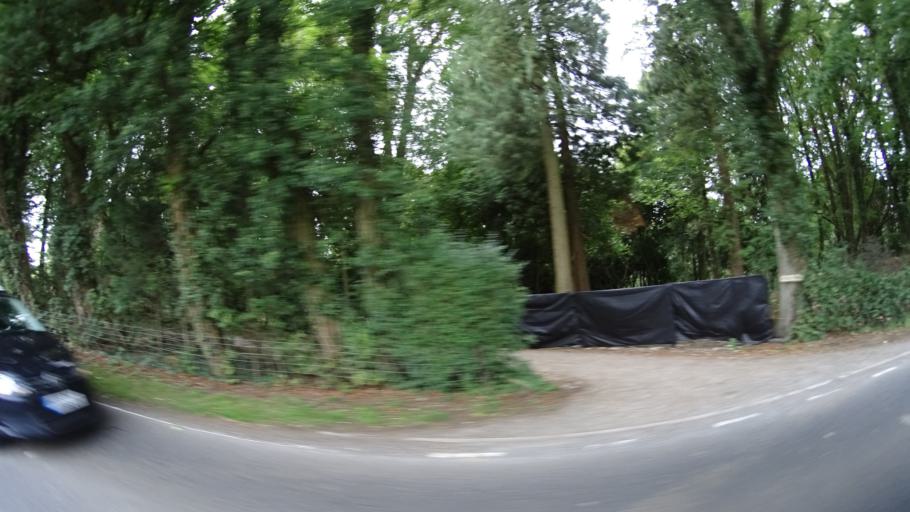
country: GB
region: England
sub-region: Dorset
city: Gillingham
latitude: 51.0408
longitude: -2.3022
